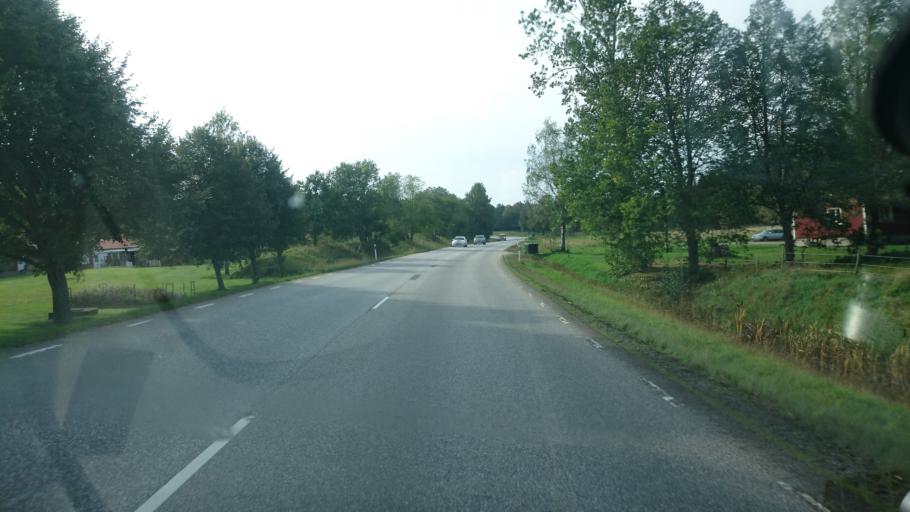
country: SE
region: Vaestra Goetaland
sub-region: Alingsas Kommun
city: Sollebrunn
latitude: 58.0863
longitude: 12.4930
